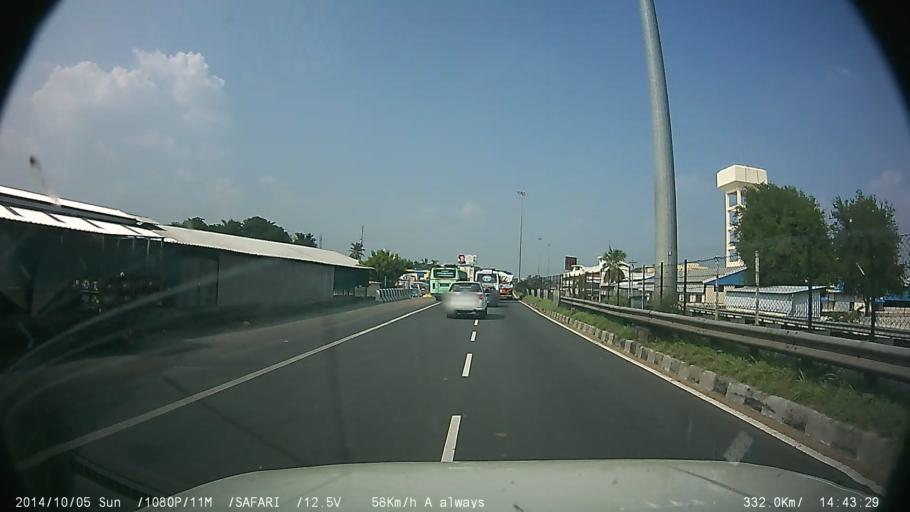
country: IN
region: Tamil Nadu
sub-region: Kancheepuram
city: Madurantakam
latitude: 12.4317
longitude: 79.8317
